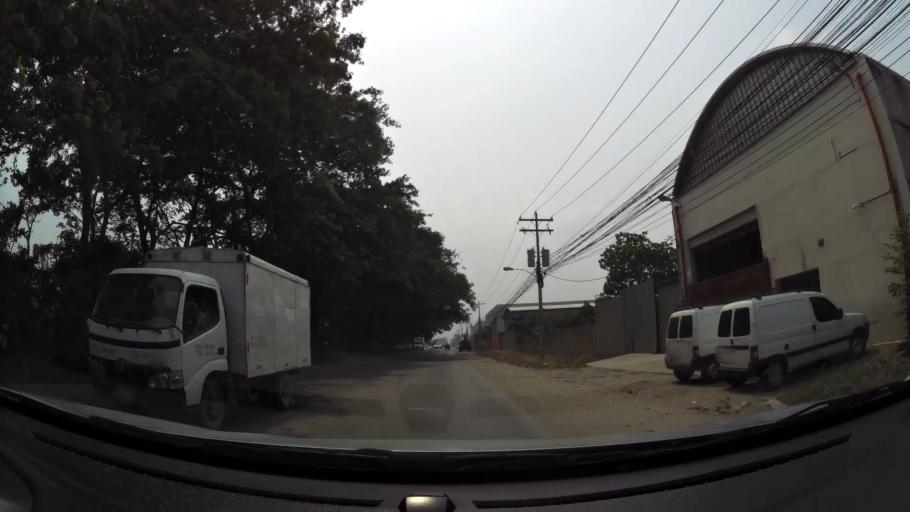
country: HN
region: Cortes
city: Chotepe
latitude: 15.4662
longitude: -87.9775
